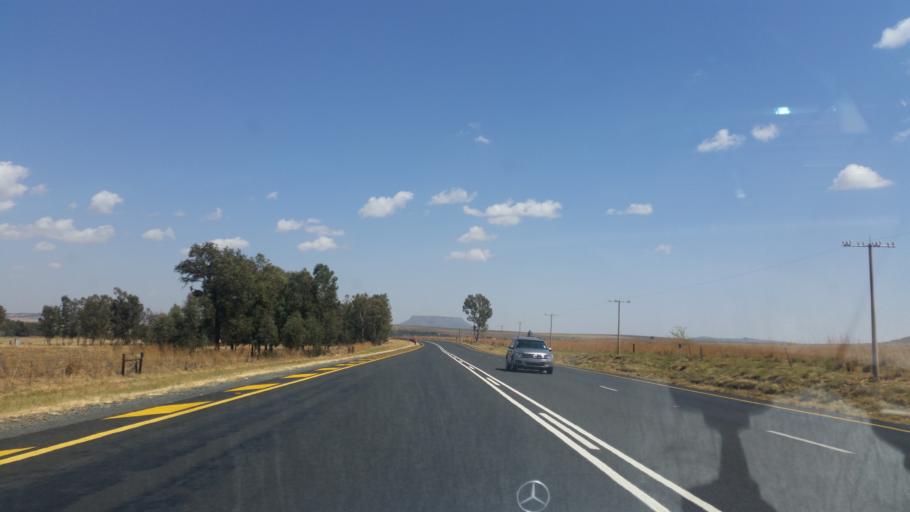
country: ZA
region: Orange Free State
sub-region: Thabo Mofutsanyana District Municipality
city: Senekal
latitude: -28.3094
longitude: 27.8879
